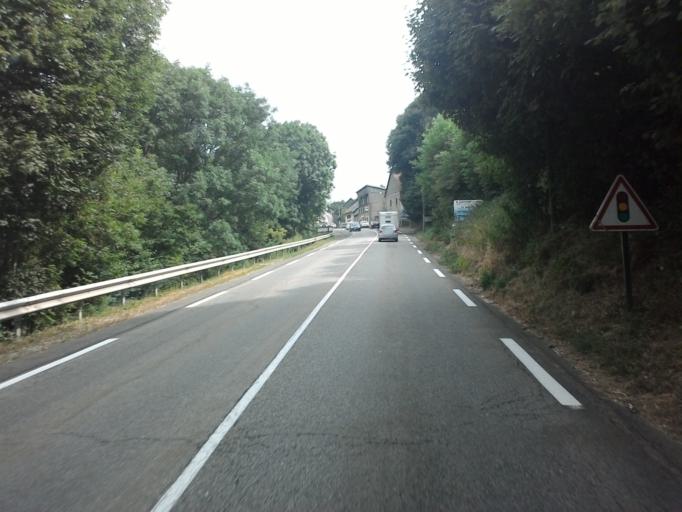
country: FR
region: Rhone-Alpes
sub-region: Departement de l'Isere
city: Pierre-Chatel
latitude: 45.0004
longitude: 5.7723
